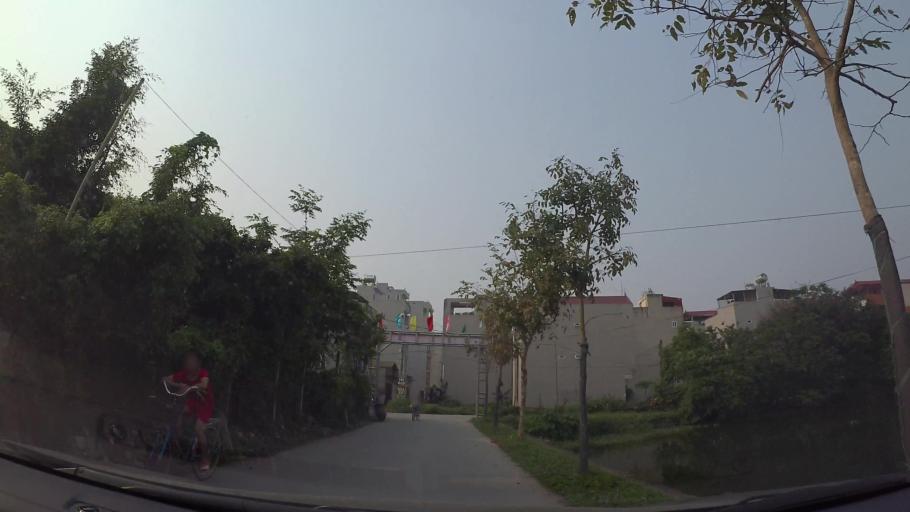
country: VN
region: Ha Noi
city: Thuong Tin
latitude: 20.8694
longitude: 105.8760
